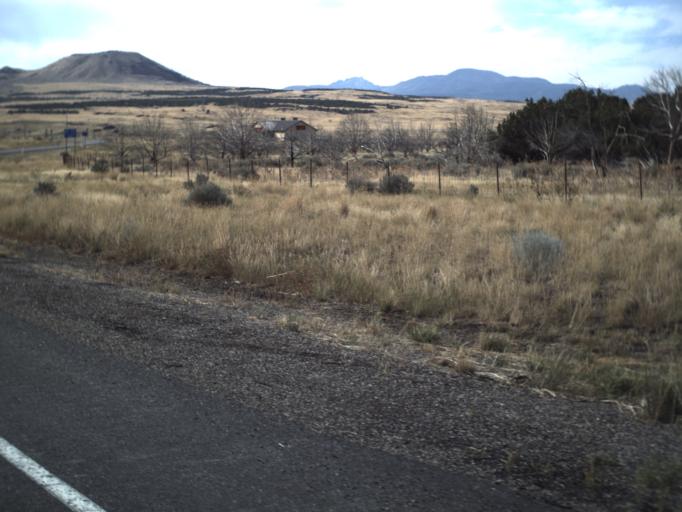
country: US
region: Utah
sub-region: Beaver County
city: Beaver
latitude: 38.6166
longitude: -112.6117
